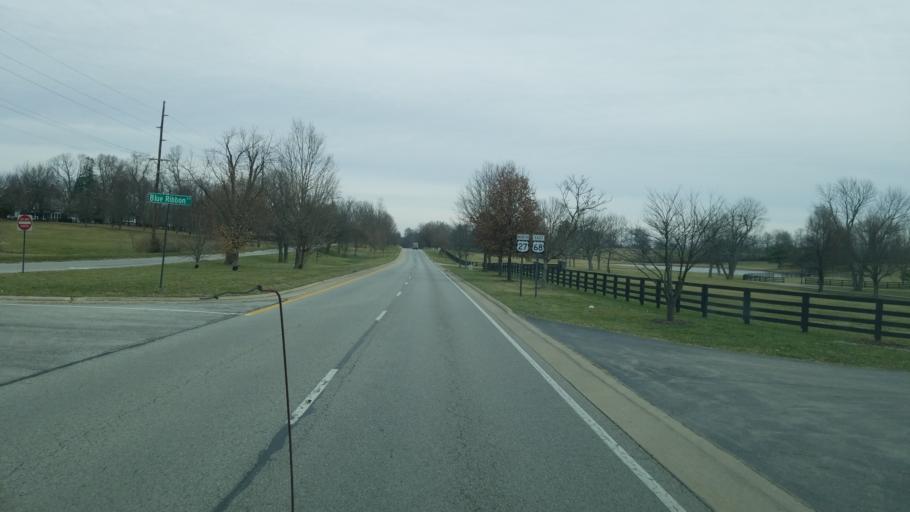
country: US
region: Kentucky
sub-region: Fayette County
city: Lexington-Fayette
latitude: 38.0875
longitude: -84.4368
